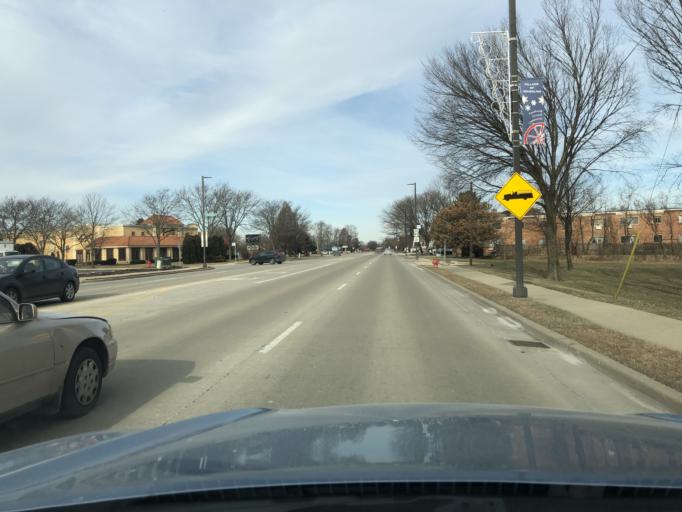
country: US
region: Illinois
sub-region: Cook County
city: Wheeling
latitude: 42.1312
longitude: -87.9012
